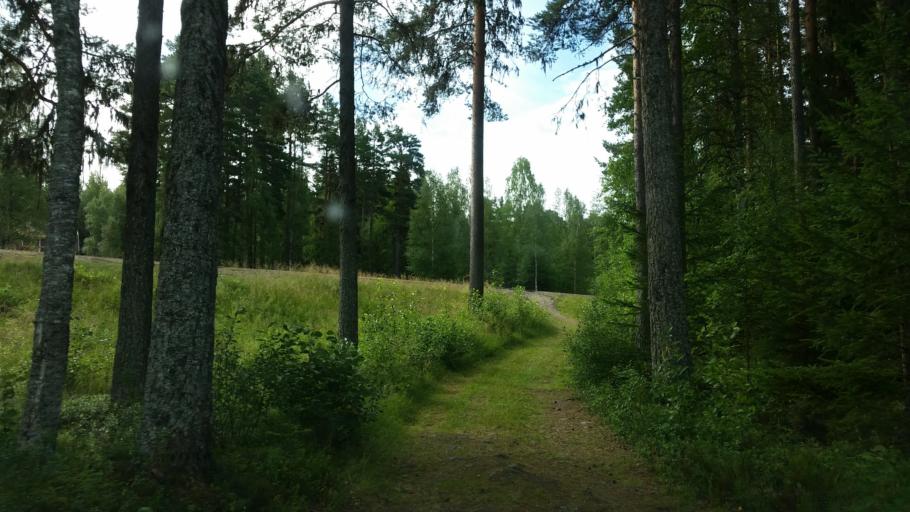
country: SE
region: Vaesternorrland
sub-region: Ange Kommun
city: Ange
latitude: 62.1912
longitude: 15.6610
